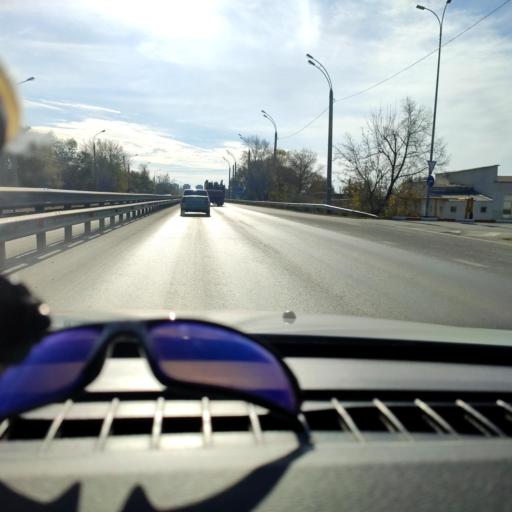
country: RU
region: Samara
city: Samara
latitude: 53.1133
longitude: 50.1658
